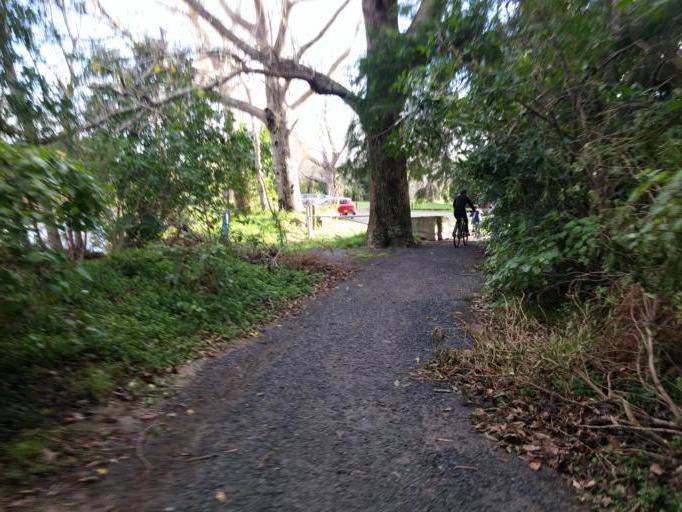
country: NZ
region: Wellington
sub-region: Kapiti Coast District
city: Paraparaumu
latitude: -40.8763
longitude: 175.0363
